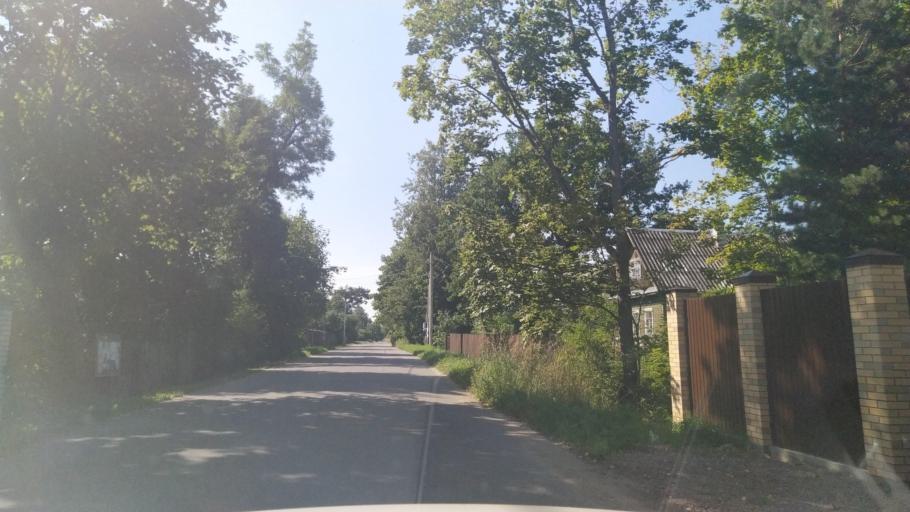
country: RU
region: Leningrad
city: Siverskiy
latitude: 59.2747
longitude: 30.0474
